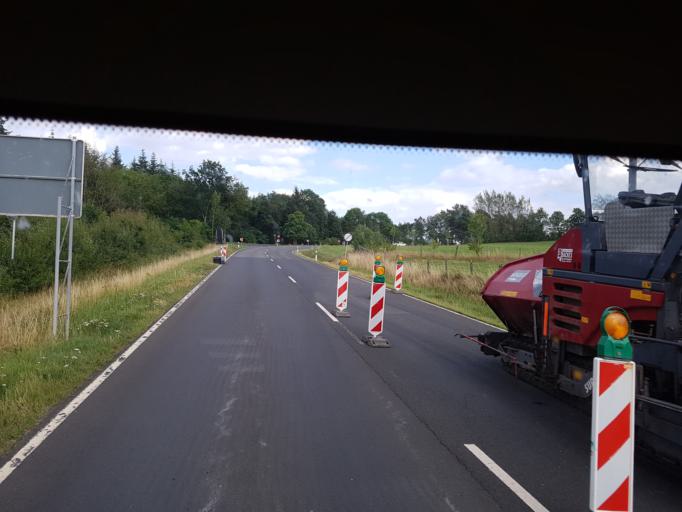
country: DE
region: Rheinland-Pfalz
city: Betteldorf
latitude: 50.2506
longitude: 6.7574
